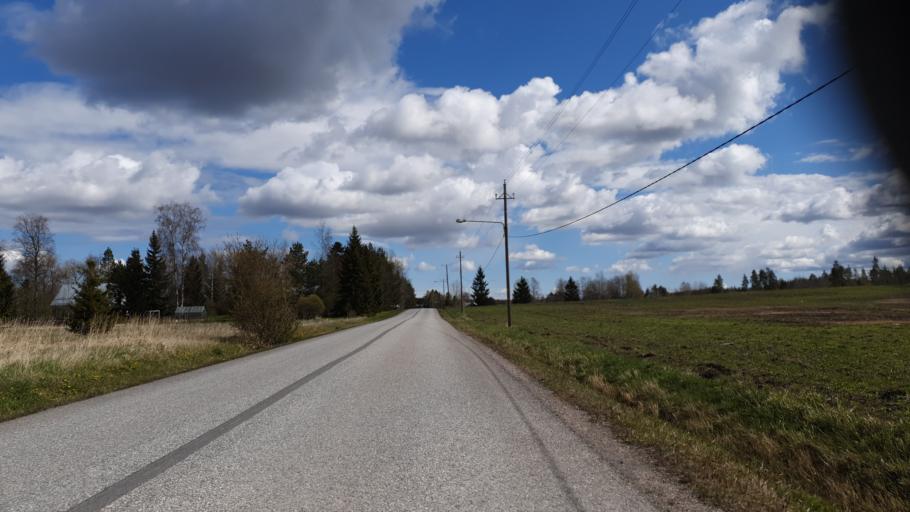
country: FI
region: Uusimaa
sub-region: Helsinki
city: Tuusula
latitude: 60.3893
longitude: 24.9061
